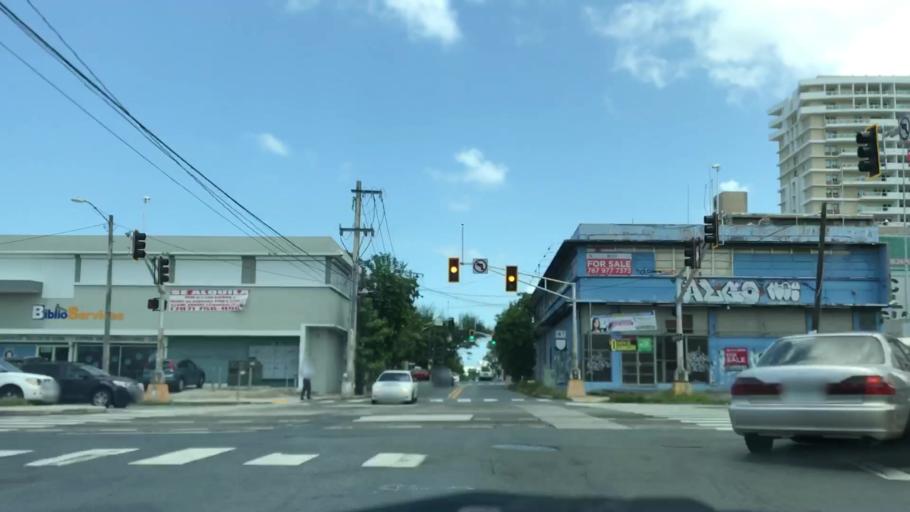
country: PR
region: Catano
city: Catano
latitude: 18.4210
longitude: -66.0577
